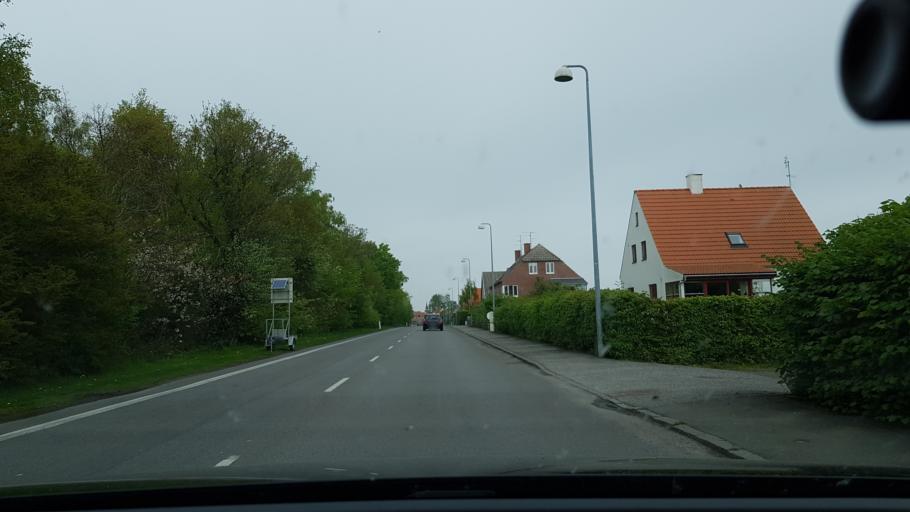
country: DK
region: Capital Region
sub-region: Bornholm Kommune
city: Nexo
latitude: 55.0539
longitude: 15.1239
